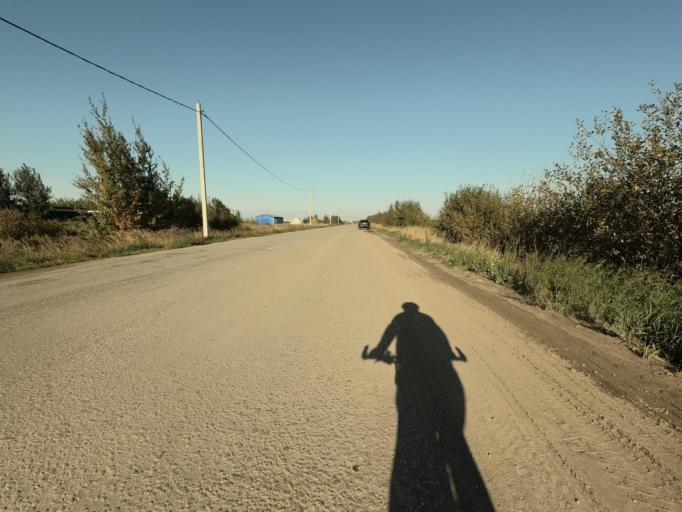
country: RU
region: St.-Petersburg
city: Petro-Slavyanka
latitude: 59.7652
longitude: 30.4863
